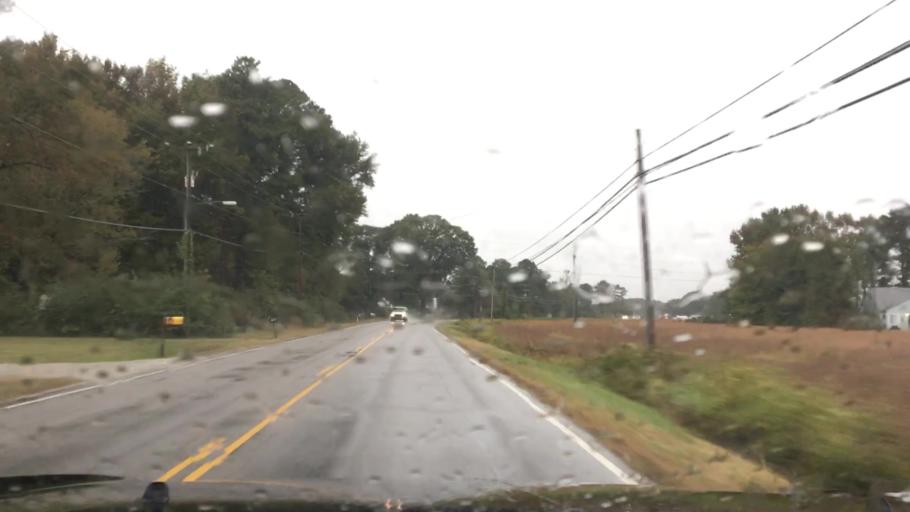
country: US
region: North Carolina
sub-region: Currituck County
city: Moyock
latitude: 36.6657
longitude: -76.2264
